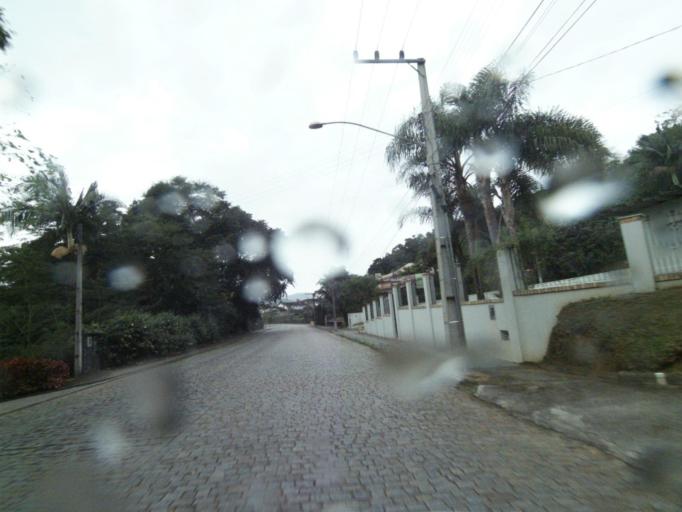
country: BR
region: Santa Catarina
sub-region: Pomerode
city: Pomerode
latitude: -26.7368
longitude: -49.1817
